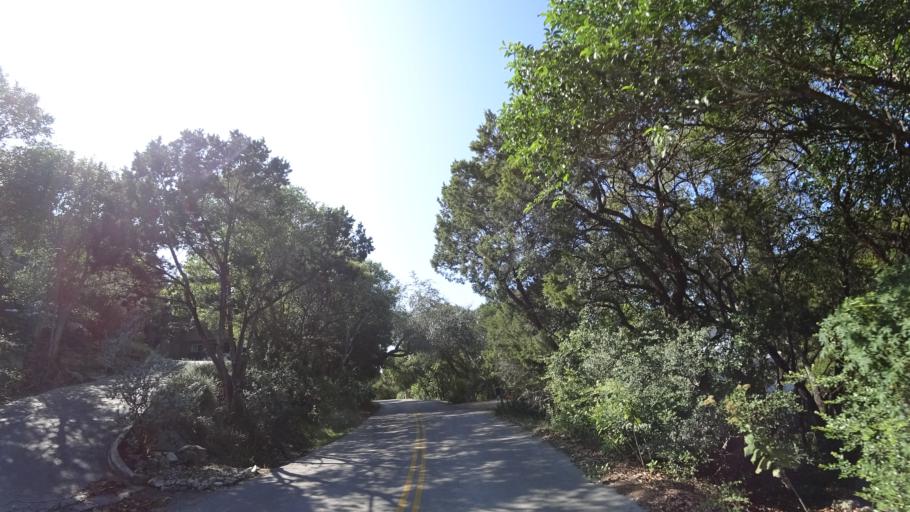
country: US
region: Texas
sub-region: Travis County
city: West Lake Hills
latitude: 30.2931
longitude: -97.8048
